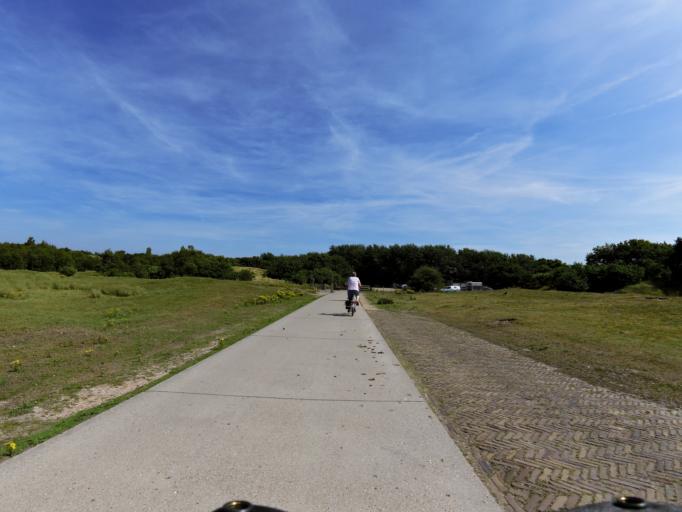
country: NL
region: Zeeland
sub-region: Schouwen-Duiveland
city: Burgh
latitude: 51.6852
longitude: 3.7159
